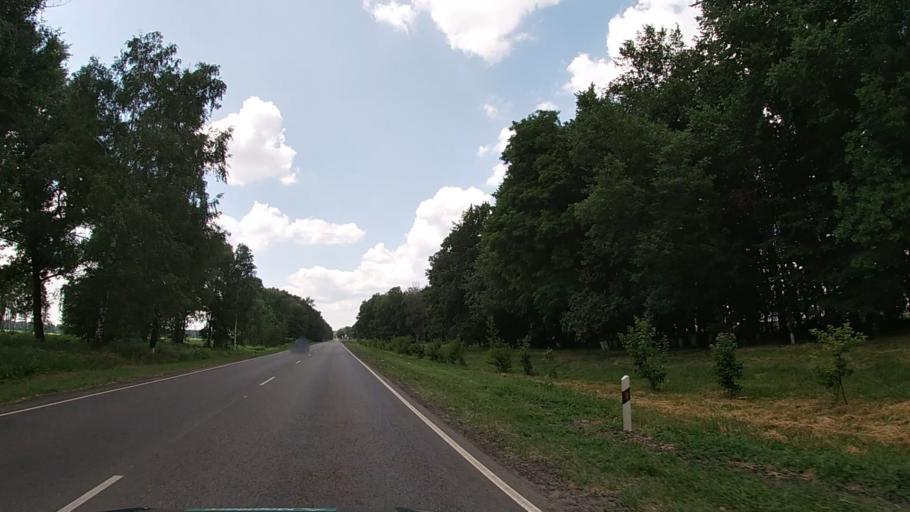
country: RU
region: Belgorod
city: Grayvoron
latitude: 50.4953
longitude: 35.7113
